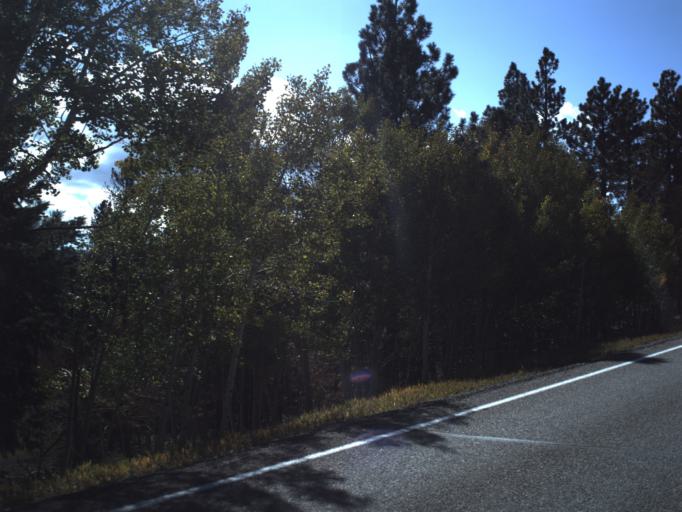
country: US
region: Utah
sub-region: Iron County
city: Parowan
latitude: 37.6546
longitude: -112.6753
